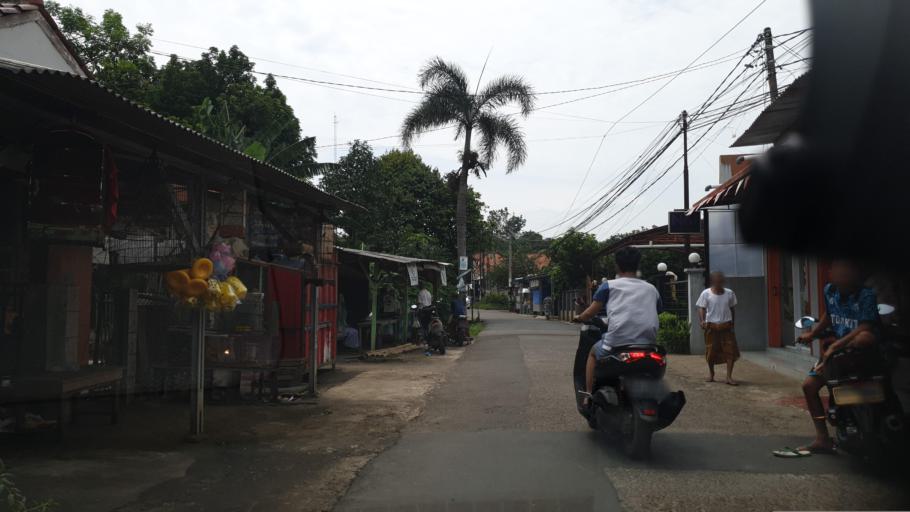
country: ID
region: West Java
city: Sawangan
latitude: -6.3778
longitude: 106.7603
